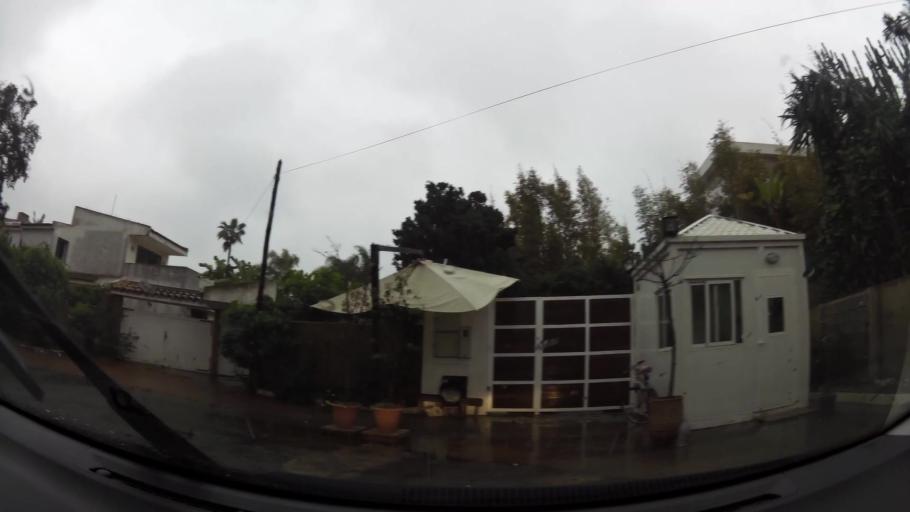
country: MA
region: Grand Casablanca
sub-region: Casablanca
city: Casablanca
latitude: 33.5916
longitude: -7.6733
